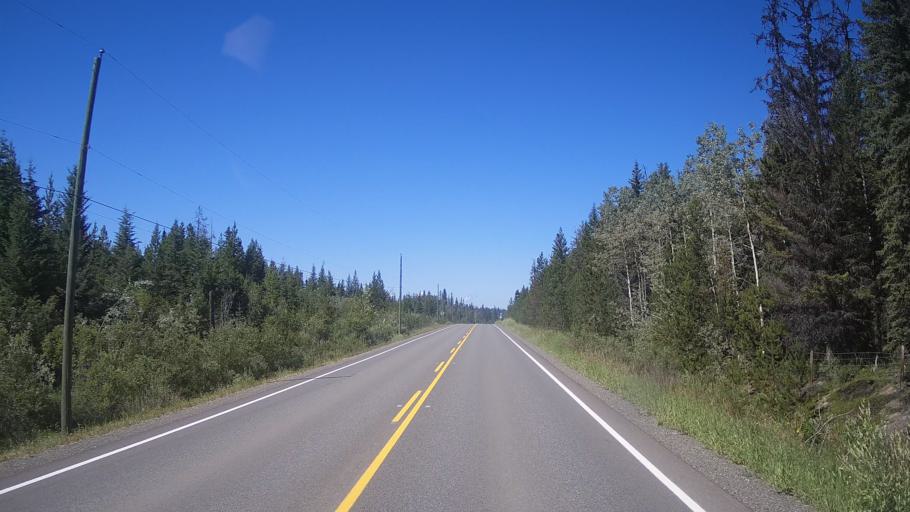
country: CA
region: British Columbia
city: Cache Creek
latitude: 51.5397
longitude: -120.9780
